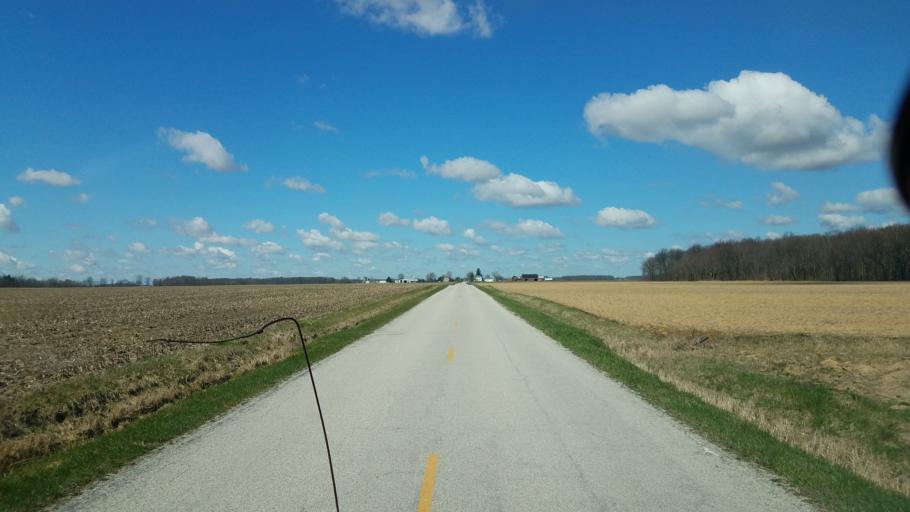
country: US
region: Ohio
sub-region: Huron County
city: Willard
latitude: 41.0229
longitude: -82.9113
